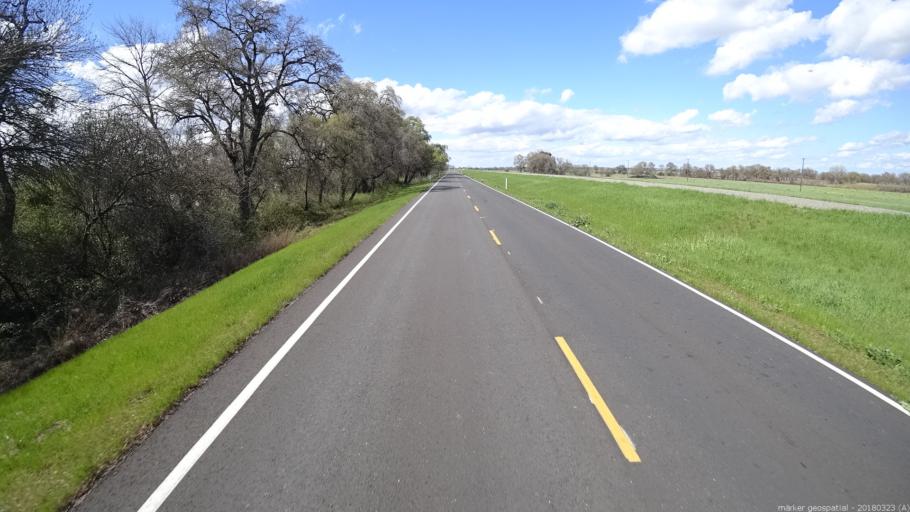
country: US
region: California
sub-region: Yolo County
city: West Sacramento
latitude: 38.6512
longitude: -121.5986
